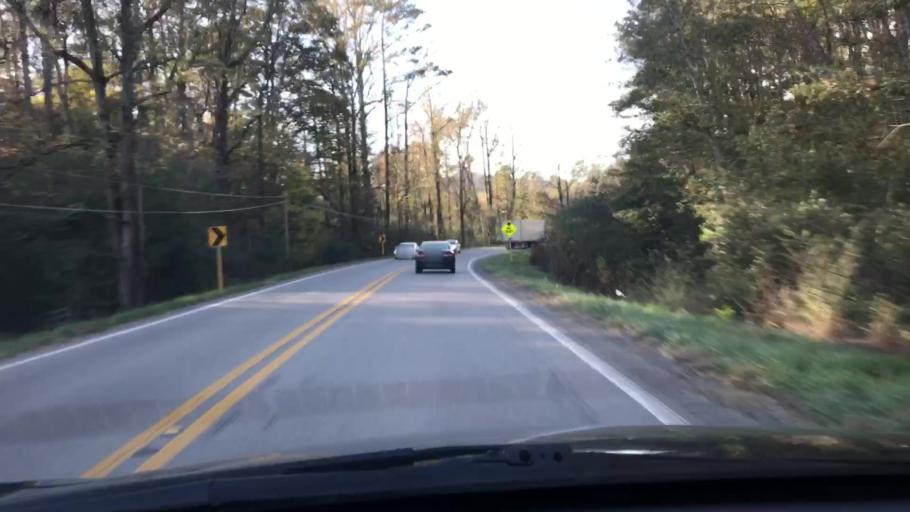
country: US
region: Alabama
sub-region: Cleburne County
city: Heflin
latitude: 33.6390
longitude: -85.6138
